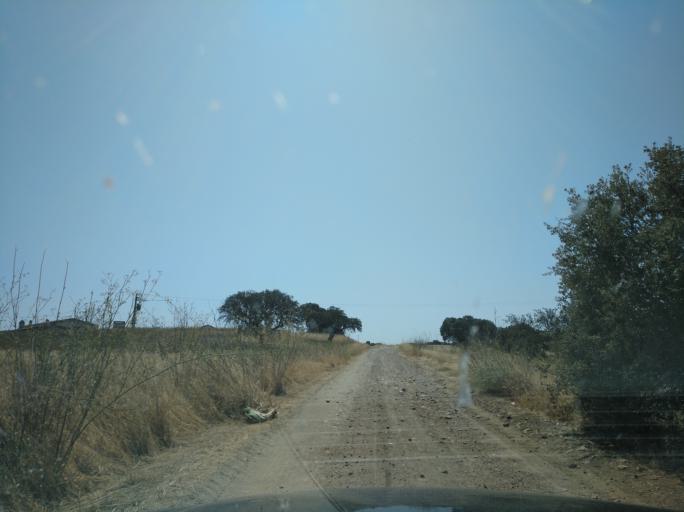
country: PT
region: Portalegre
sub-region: Campo Maior
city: Campo Maior
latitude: 39.0304
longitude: -6.9795
